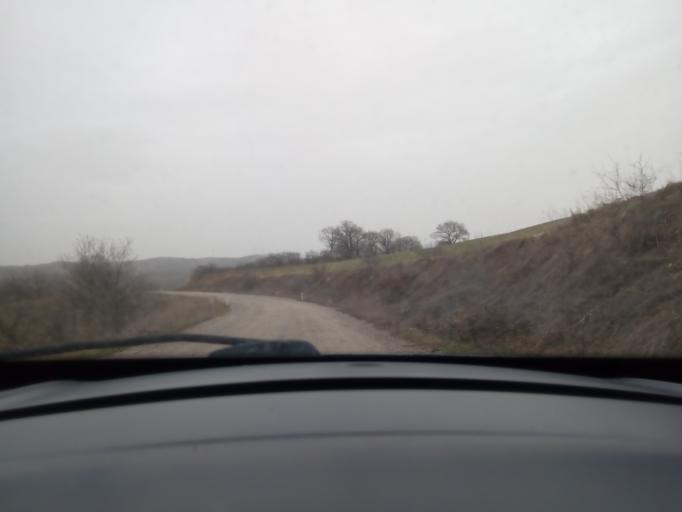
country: TR
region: Balikesir
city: Susurluk
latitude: 39.9195
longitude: 28.0806
